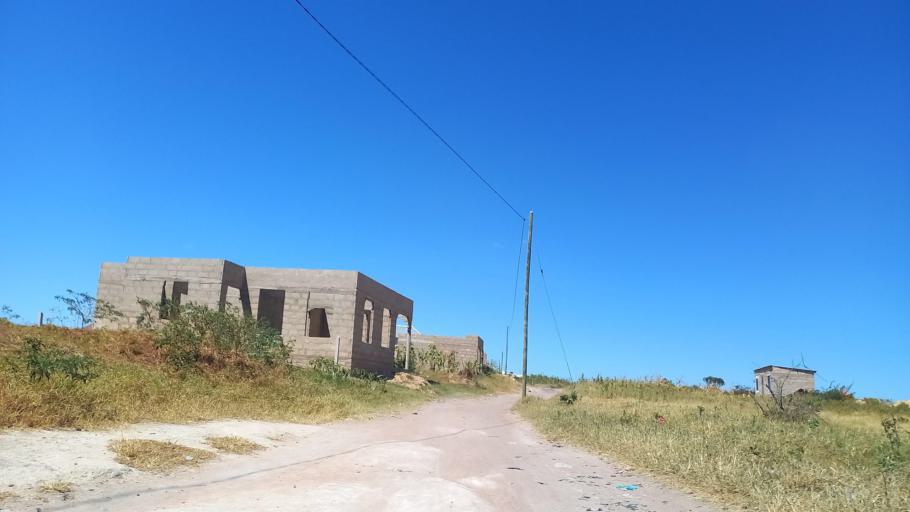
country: TZ
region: Dodoma
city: Dodoma
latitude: -6.1321
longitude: 35.6961
